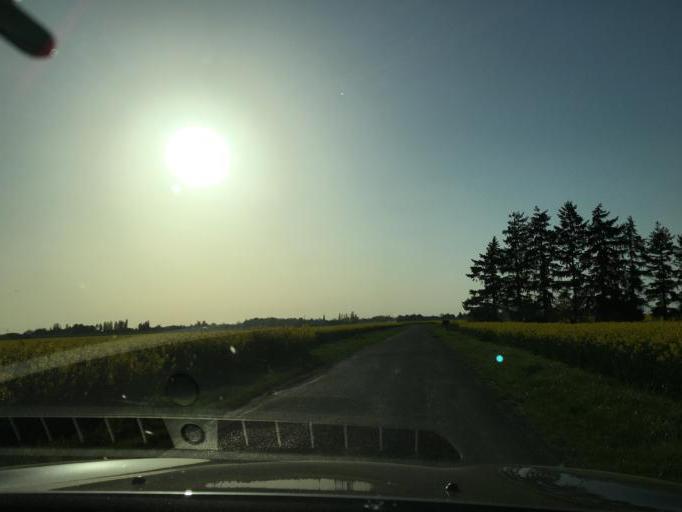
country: FR
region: Centre
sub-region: Departement du Loir-et-Cher
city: Ouzouer-le-Marche
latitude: 47.9080
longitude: 1.5500
